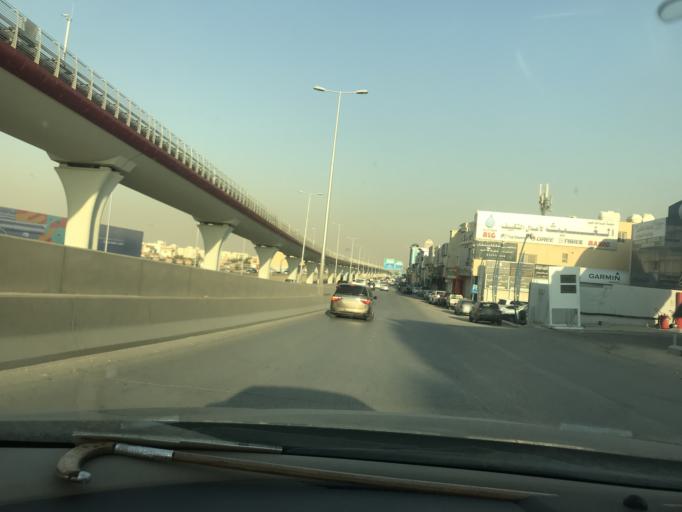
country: SA
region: Ar Riyad
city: Riyadh
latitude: 24.7600
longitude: 46.7401
